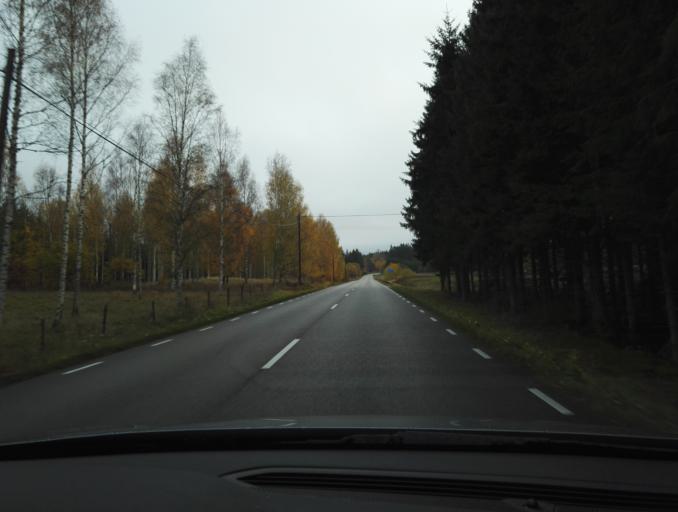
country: SE
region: Kronoberg
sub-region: Vaxjo Kommun
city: Rottne
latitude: 57.0321
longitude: 14.7901
